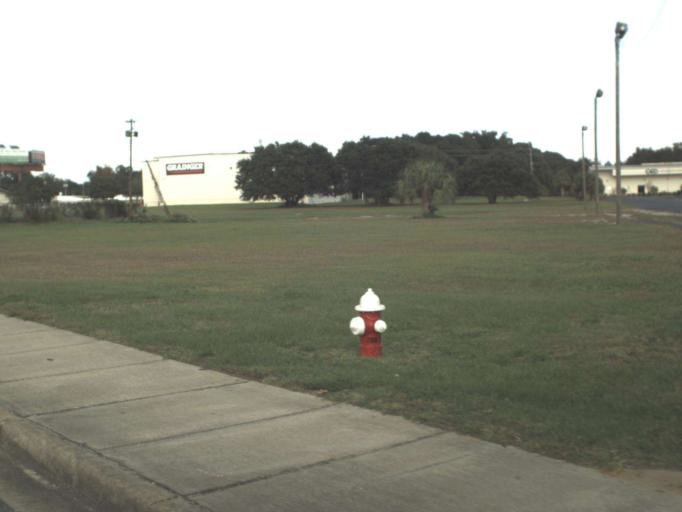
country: US
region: Florida
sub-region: Escambia County
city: Brent
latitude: 30.4560
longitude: -87.2402
